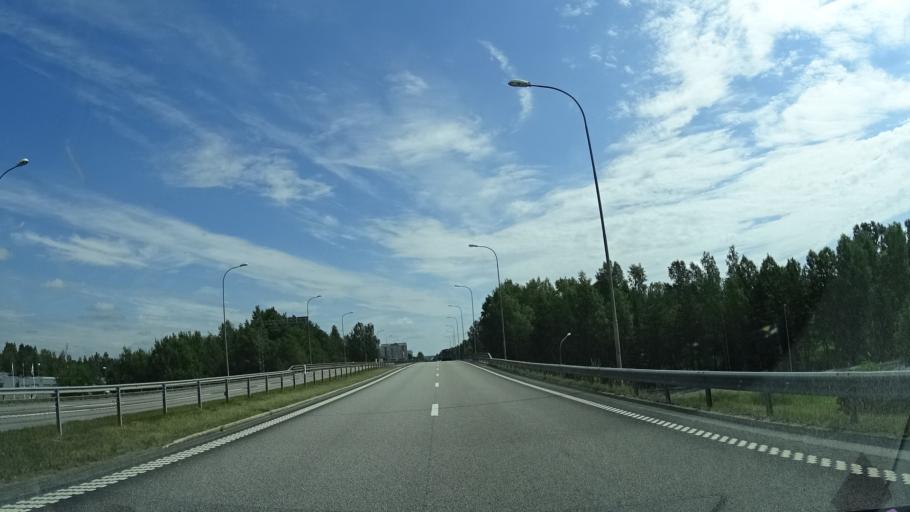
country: SE
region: OErebro
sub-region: Karlskoga Kommun
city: Karlskoga
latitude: 59.3232
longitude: 14.4782
